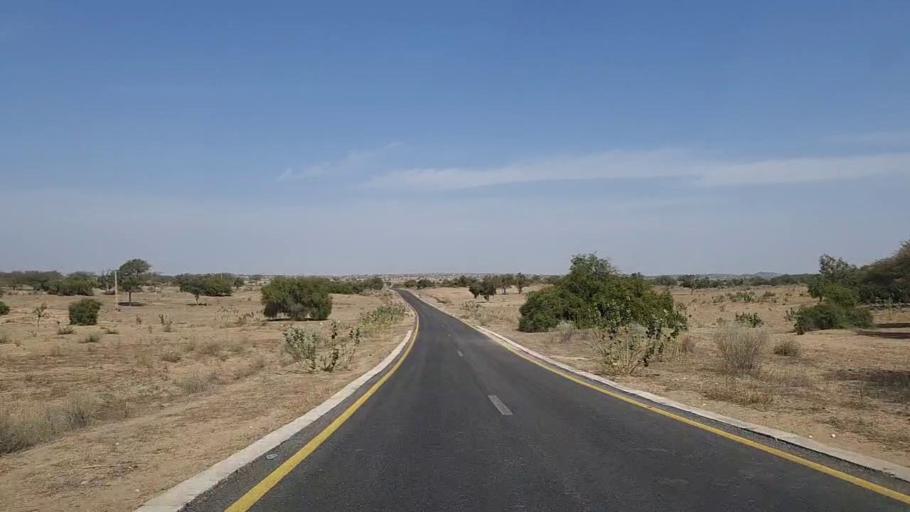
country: PK
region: Sindh
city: Mithi
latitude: 24.9118
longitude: 69.8901
